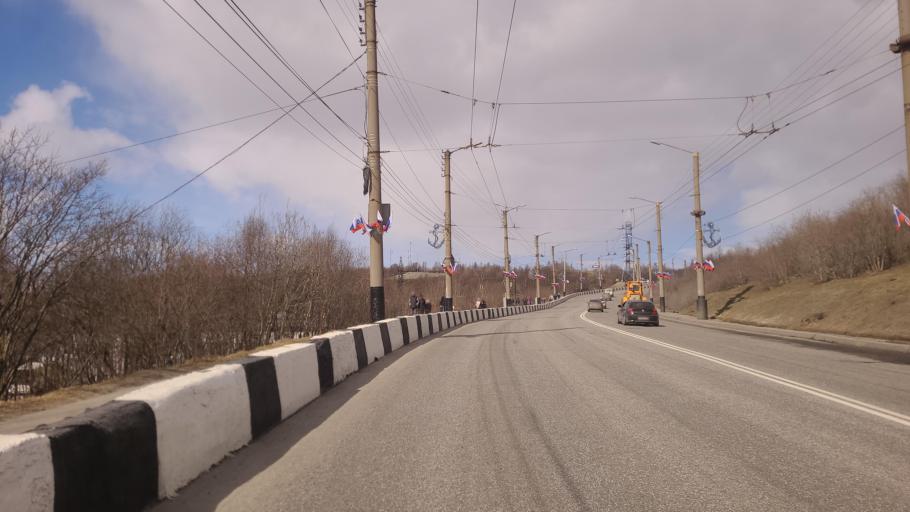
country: RU
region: Murmansk
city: Murmansk
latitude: 68.9847
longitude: 33.0922
